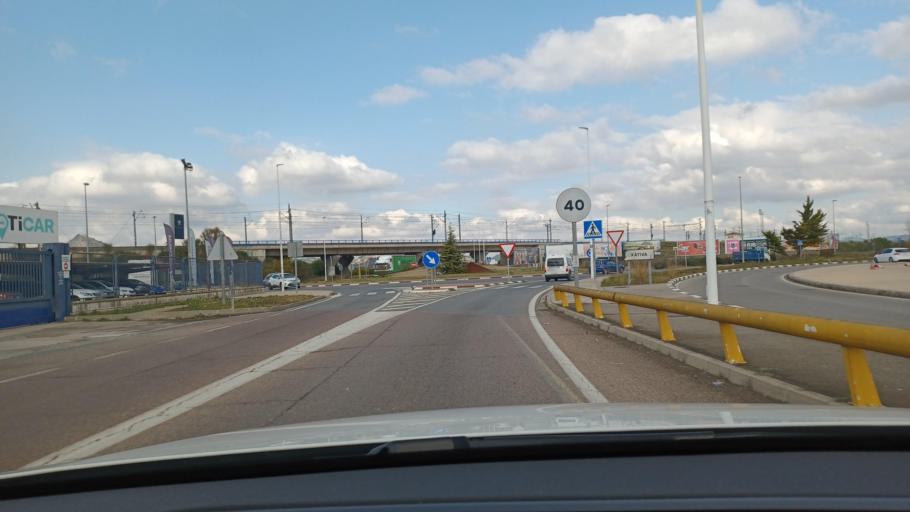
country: ES
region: Valencia
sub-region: Provincia de Valencia
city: Xativa
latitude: 38.9971
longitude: -0.5130
